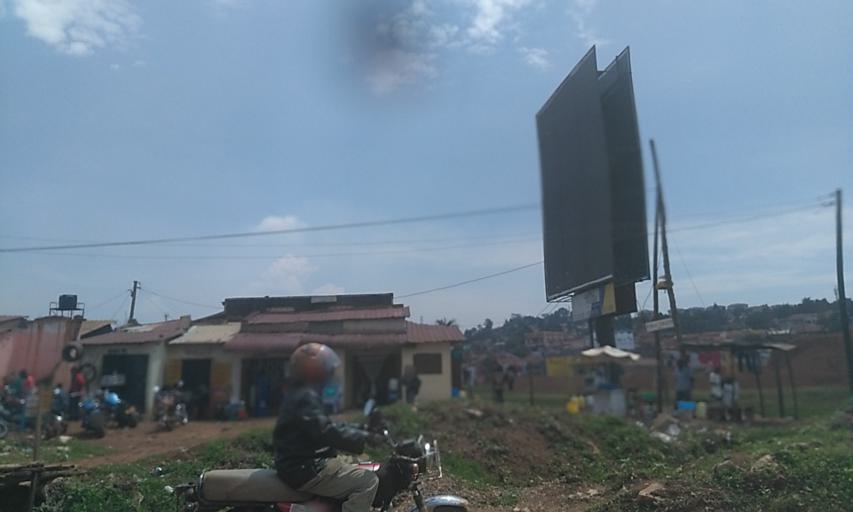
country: UG
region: Central Region
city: Kampala Central Division
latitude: 0.3453
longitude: 32.5437
